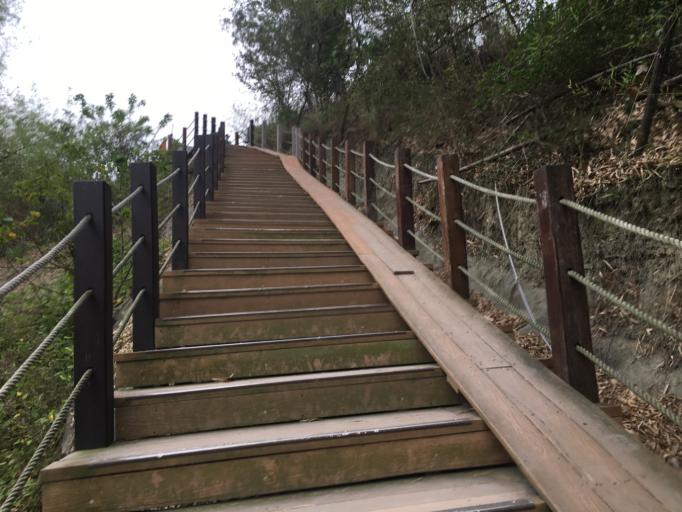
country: TW
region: Taiwan
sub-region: Tainan
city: Tainan
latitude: 22.8896
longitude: 120.3890
